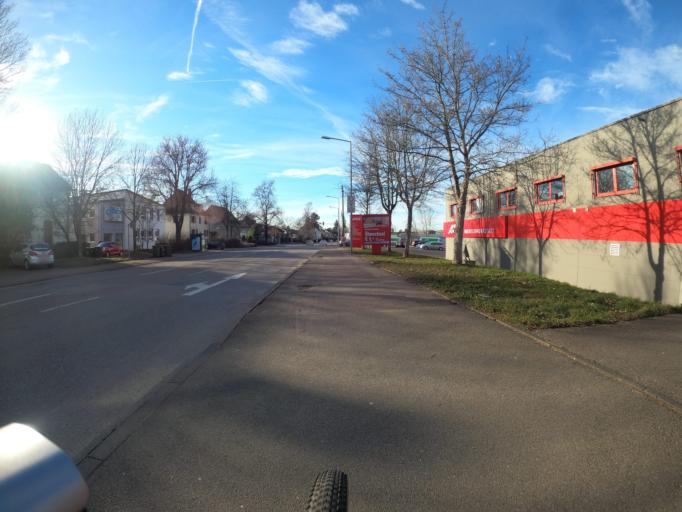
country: DE
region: Baden-Wuerttemberg
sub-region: Regierungsbezirk Stuttgart
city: Kirchheim unter Teck
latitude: 48.6536
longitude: 9.4348
